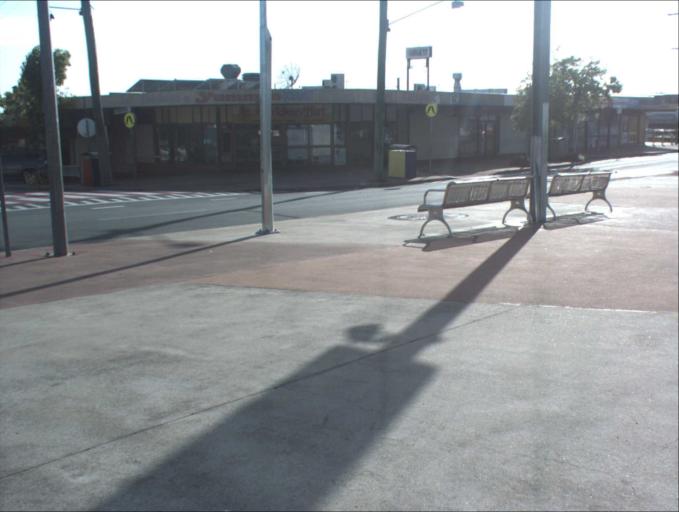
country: AU
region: Queensland
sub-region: Logan
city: Logan City
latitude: -27.6381
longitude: 153.1039
